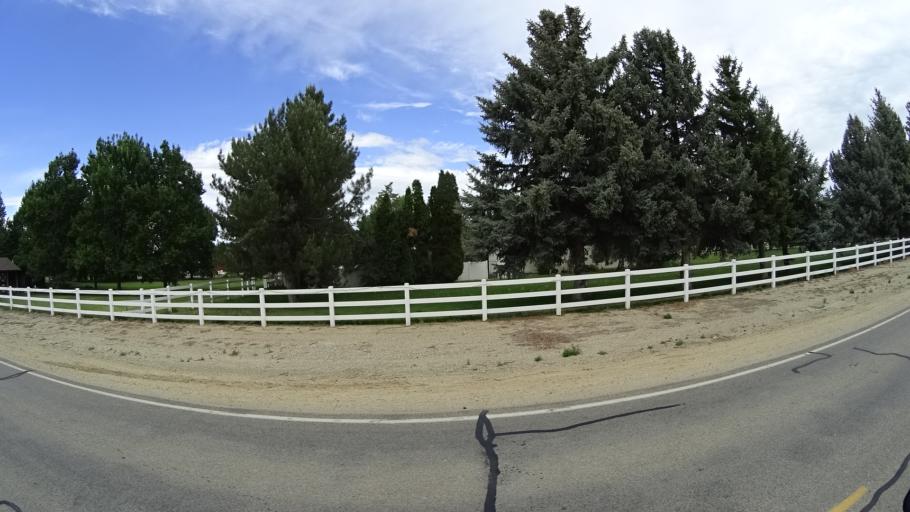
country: US
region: Idaho
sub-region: Ada County
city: Meridian
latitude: 43.5757
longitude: -116.3399
